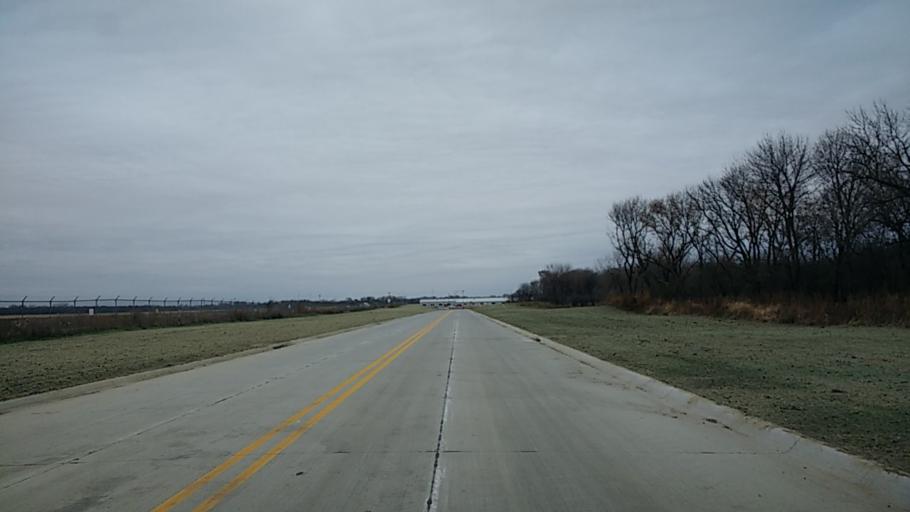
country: US
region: Iowa
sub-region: Woodbury County
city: Sergeant Bluff
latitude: 42.4185
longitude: -96.3792
